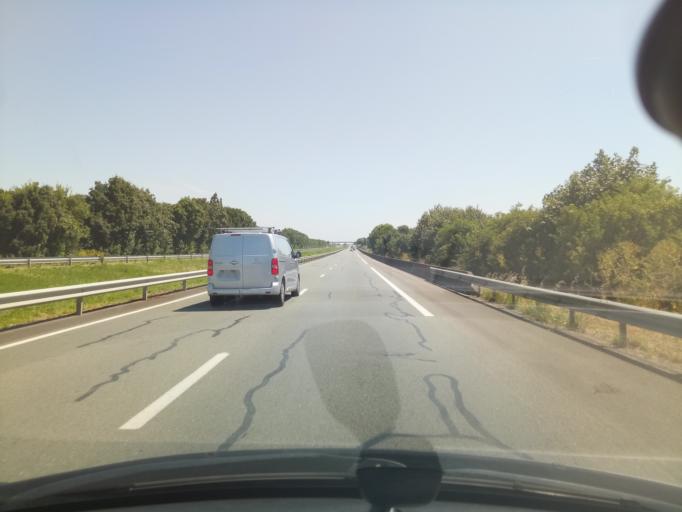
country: FR
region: Poitou-Charentes
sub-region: Departement de la Charente-Maritime
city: Sainte-Soulle
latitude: 46.2111
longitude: -0.9995
